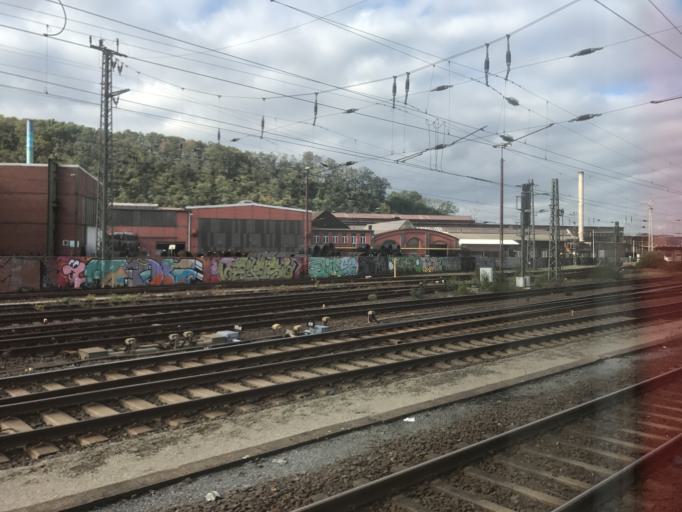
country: DE
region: North Rhine-Westphalia
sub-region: Regierungsbezirk Arnsberg
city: Hagen
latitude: 51.3598
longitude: 7.4598
